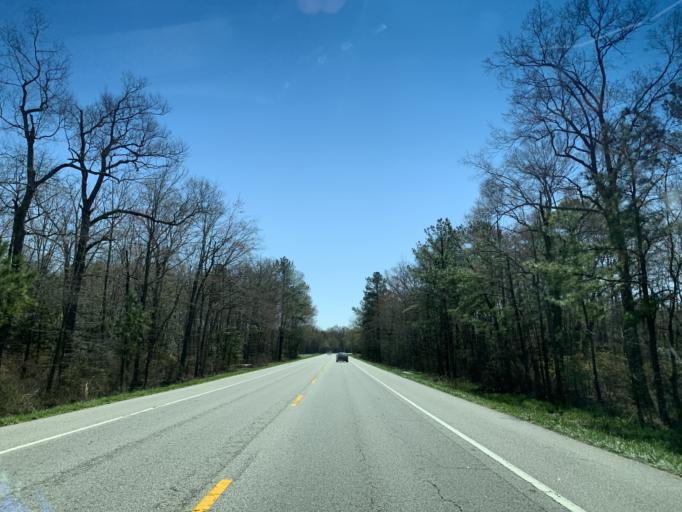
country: US
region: Maryland
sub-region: Queen Anne's County
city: Centreville
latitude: 38.9740
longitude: -76.0050
